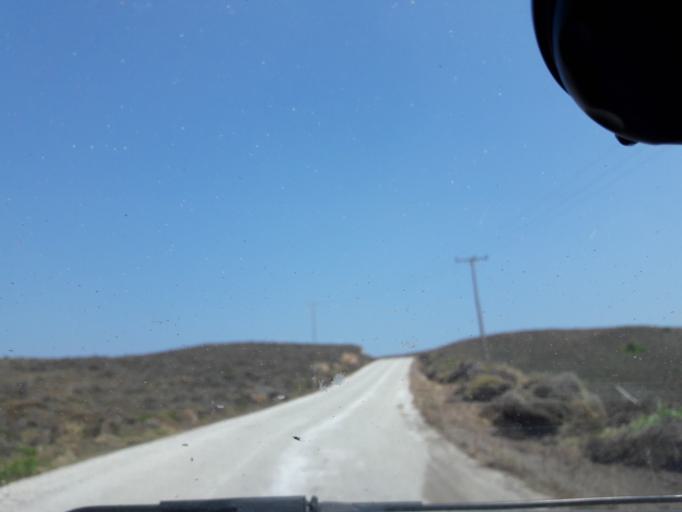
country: GR
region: North Aegean
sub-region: Nomos Lesvou
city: Myrina
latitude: 39.9787
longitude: 25.3439
